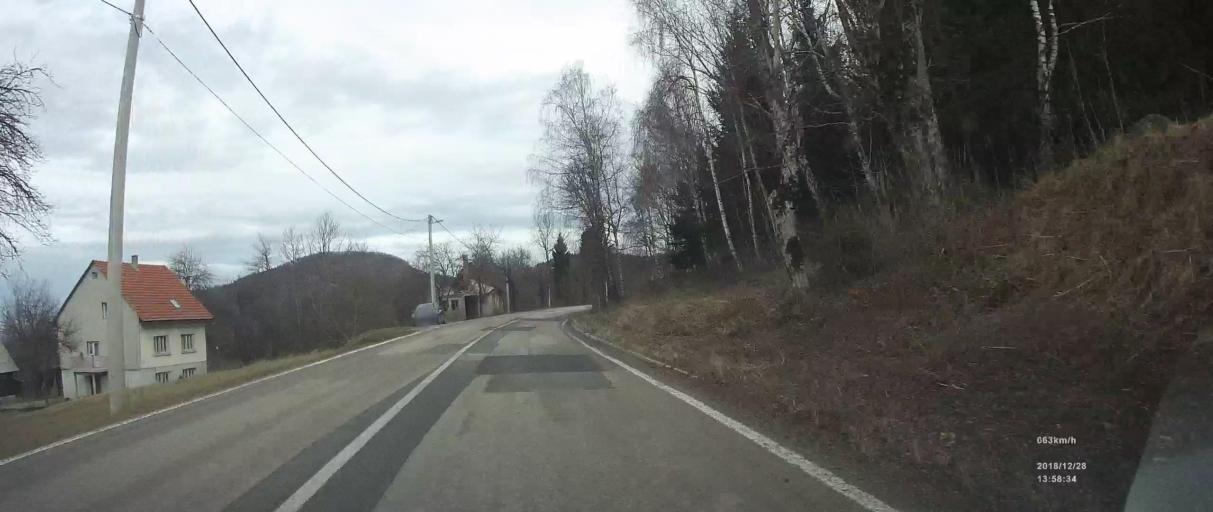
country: HR
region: Primorsko-Goranska
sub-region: Grad Delnice
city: Delnice
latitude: 45.3977
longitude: 14.9005
